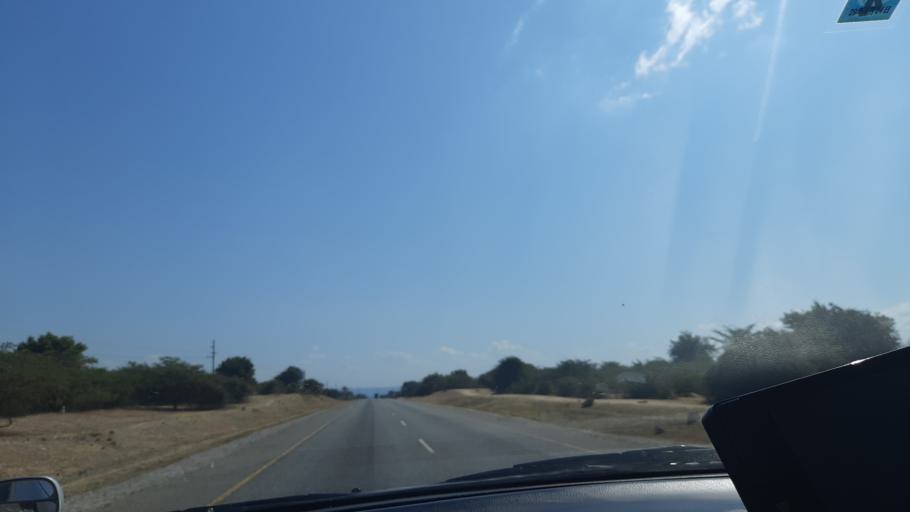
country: TZ
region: Singida
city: Kintinku
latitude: -5.8796
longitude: 35.1293
